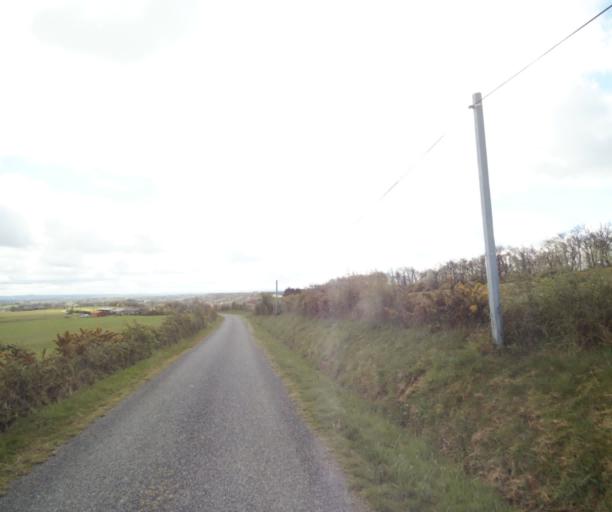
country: FR
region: Midi-Pyrenees
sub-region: Departement de l'Ariege
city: Saverdun
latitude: 43.2293
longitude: 1.5277
